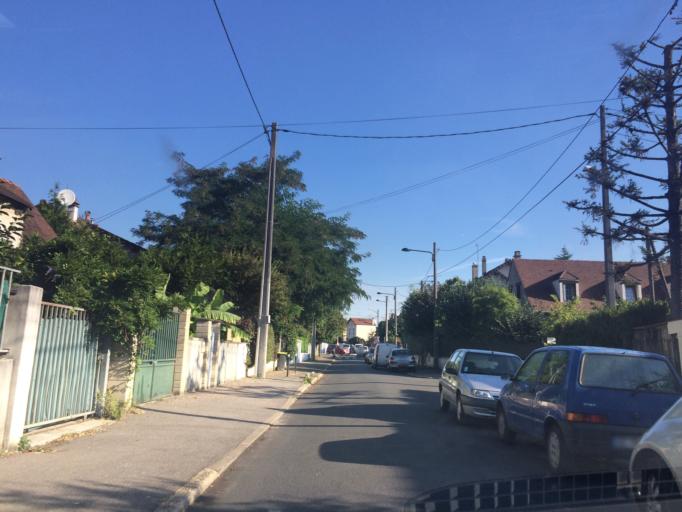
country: FR
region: Ile-de-France
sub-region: Departement du Val-de-Marne
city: Chennevieres-sur-Marne
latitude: 48.8110
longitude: 2.5475
